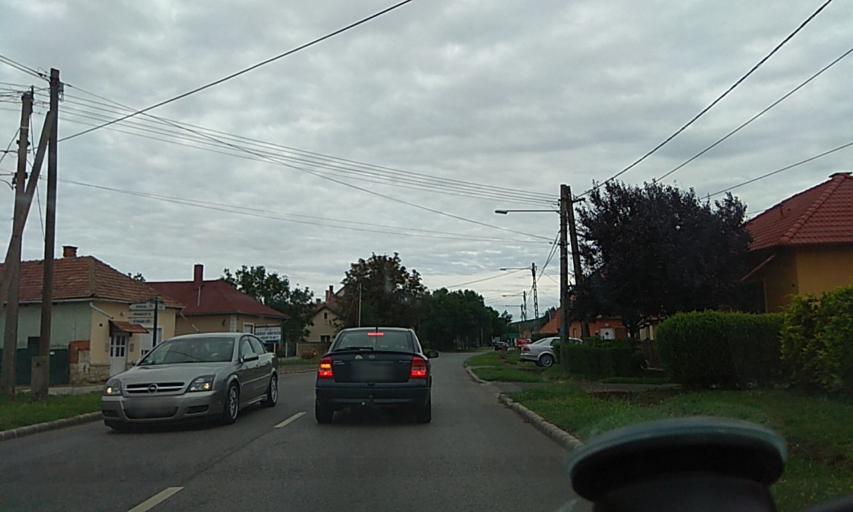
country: HU
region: Borsod-Abauj-Zemplen
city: Tarcal
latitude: 48.1321
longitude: 21.3424
